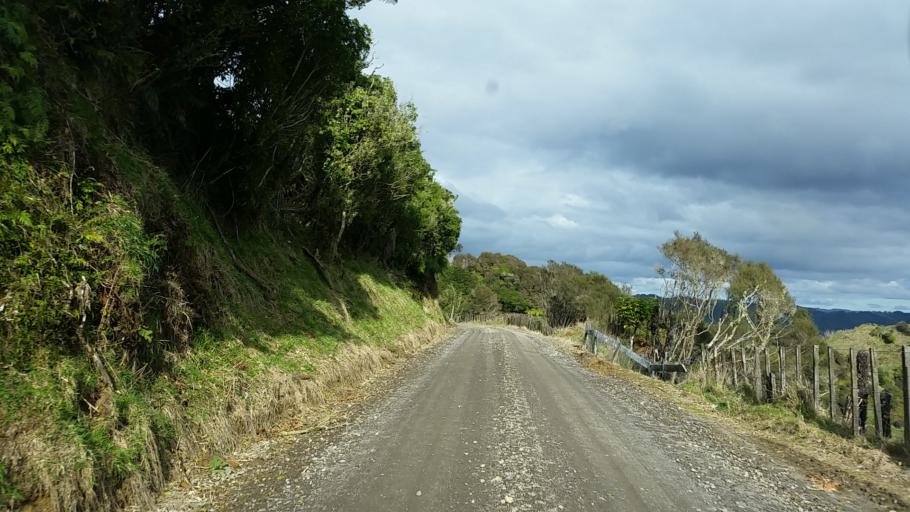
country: NZ
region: Taranaki
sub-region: South Taranaki District
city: Eltham
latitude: -39.1735
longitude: 174.6272
